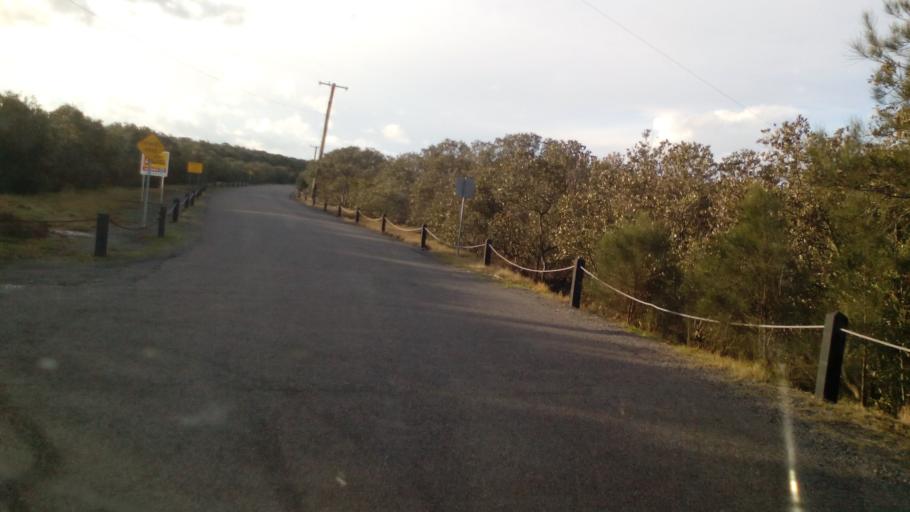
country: AU
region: New South Wales
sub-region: Newcastle
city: Mayfield West
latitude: -32.8471
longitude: 151.6973
